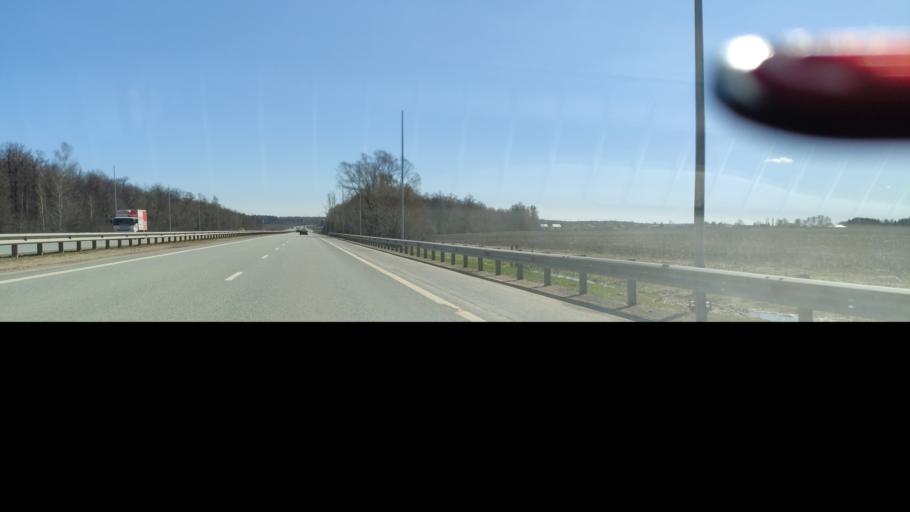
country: RU
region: Bashkortostan
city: Kabakovo
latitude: 54.4499
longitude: 55.9184
